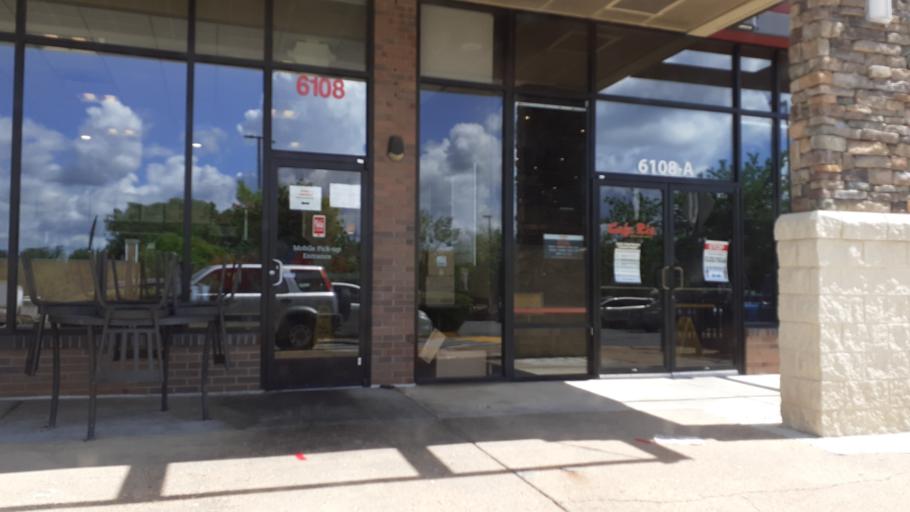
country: US
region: Virginia
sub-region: Fairfax County
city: Seven Corners
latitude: 38.8686
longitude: -77.1441
